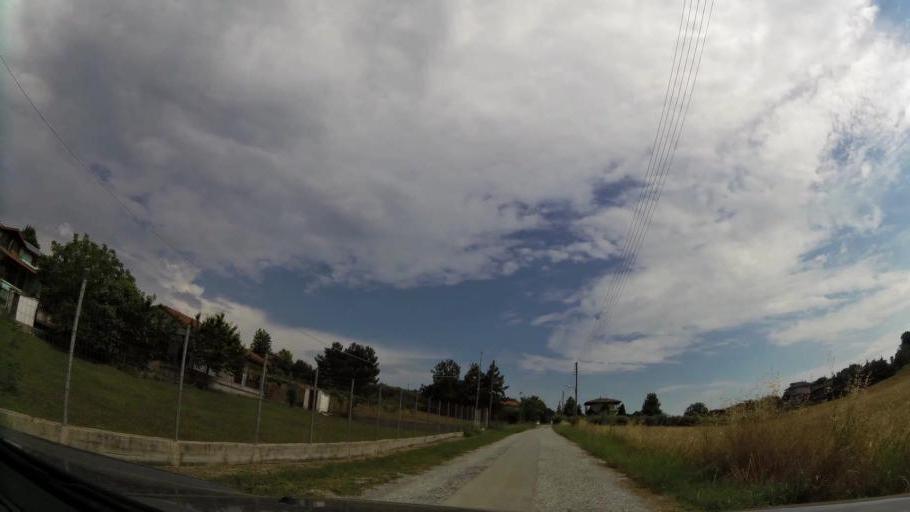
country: GR
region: Central Macedonia
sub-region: Nomos Pierias
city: Makrygialos
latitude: 40.4235
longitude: 22.6051
